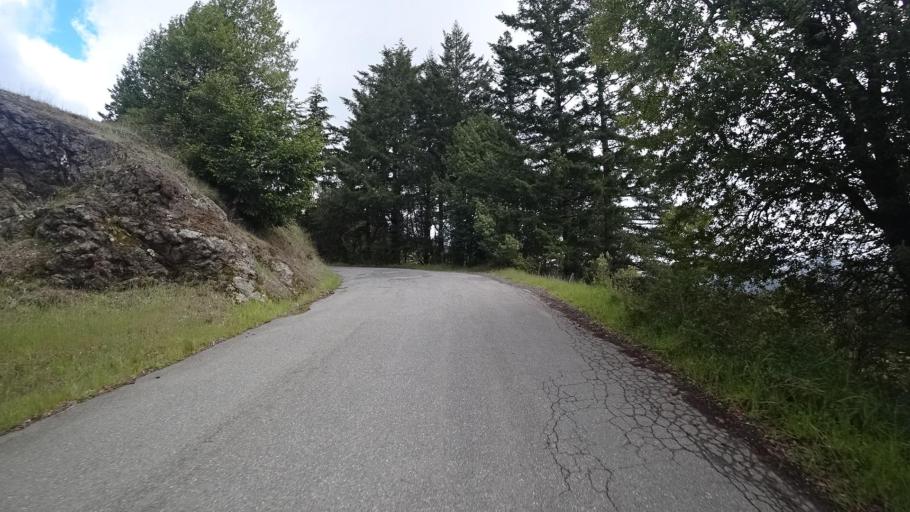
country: US
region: California
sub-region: Humboldt County
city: Blue Lake
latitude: 40.8566
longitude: -123.9149
